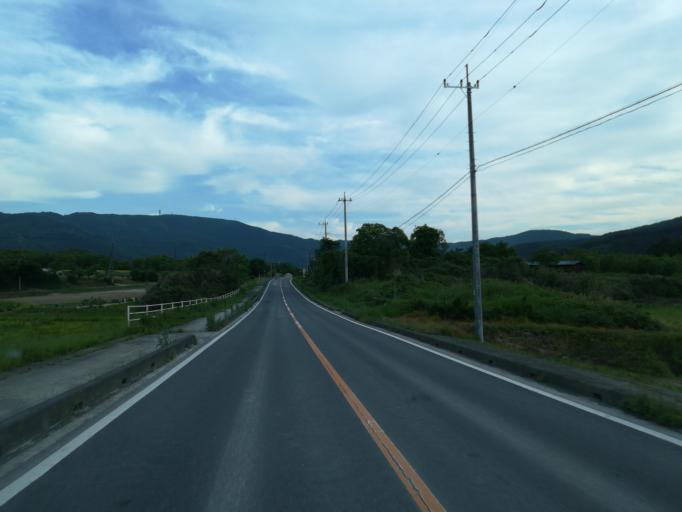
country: JP
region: Ibaraki
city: Tsukuba
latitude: 36.2020
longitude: 140.1788
